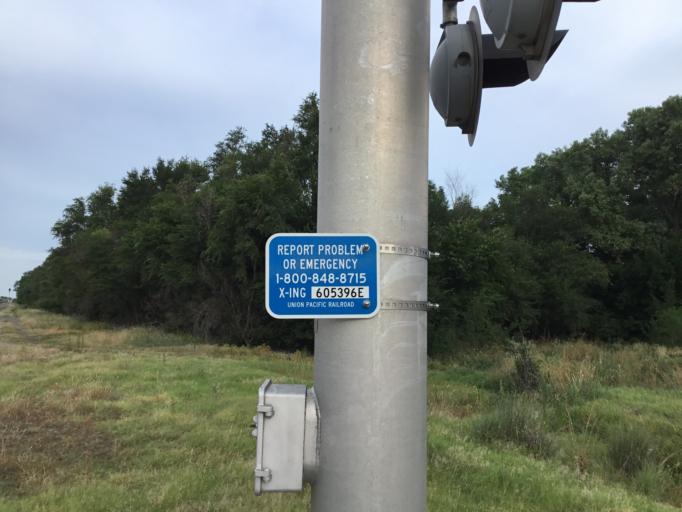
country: US
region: Kansas
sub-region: Stafford County
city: Stafford
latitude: 37.7601
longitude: -98.5566
